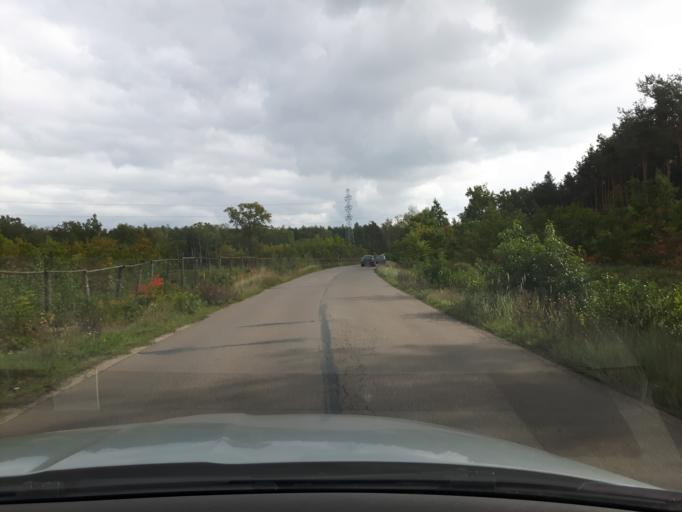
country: PL
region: Masovian Voivodeship
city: Zielonka
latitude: 52.2993
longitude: 21.1338
